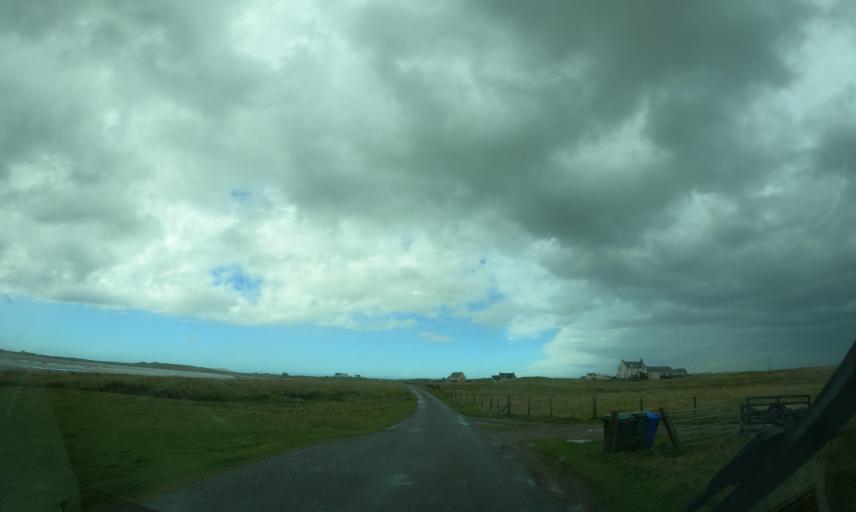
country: GB
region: Scotland
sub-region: Eilean Siar
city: Barra
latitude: 56.5256
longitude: -6.7992
